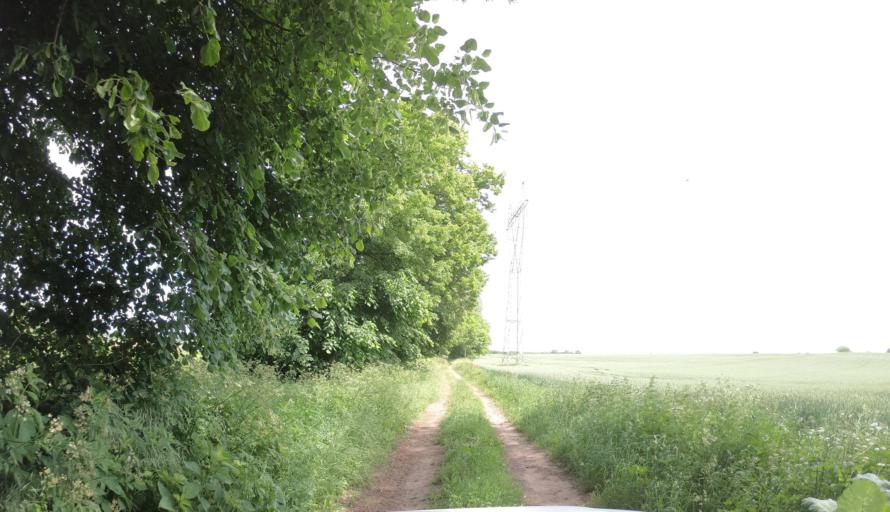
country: PL
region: West Pomeranian Voivodeship
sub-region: Powiat goleniowski
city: Przybiernow
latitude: 53.8258
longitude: 14.7184
